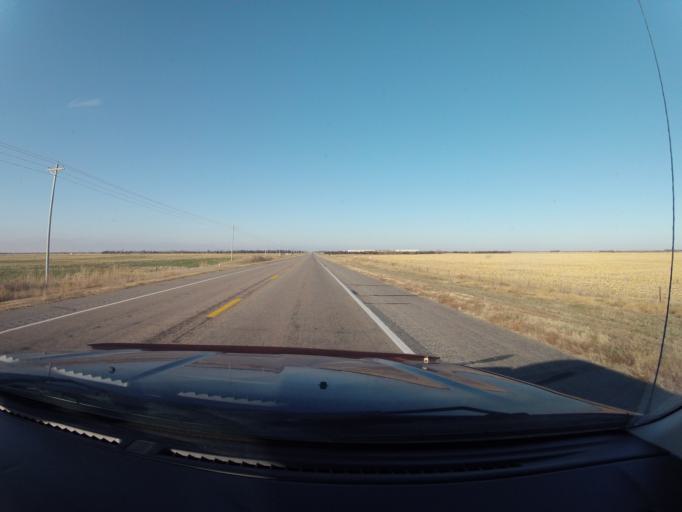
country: US
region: Nebraska
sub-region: Kearney County
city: Minden
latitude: 40.6214
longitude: -98.9515
